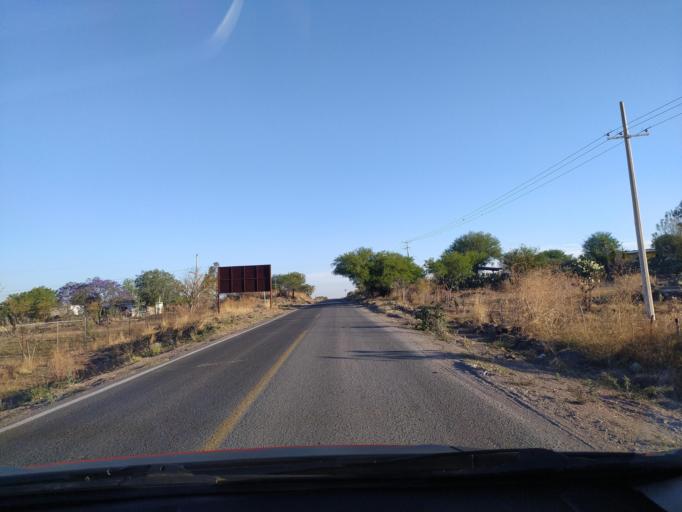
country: MX
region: Guanajuato
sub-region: San Francisco del Rincon
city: San Ignacio de Hidalgo
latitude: 20.8209
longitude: -101.8414
